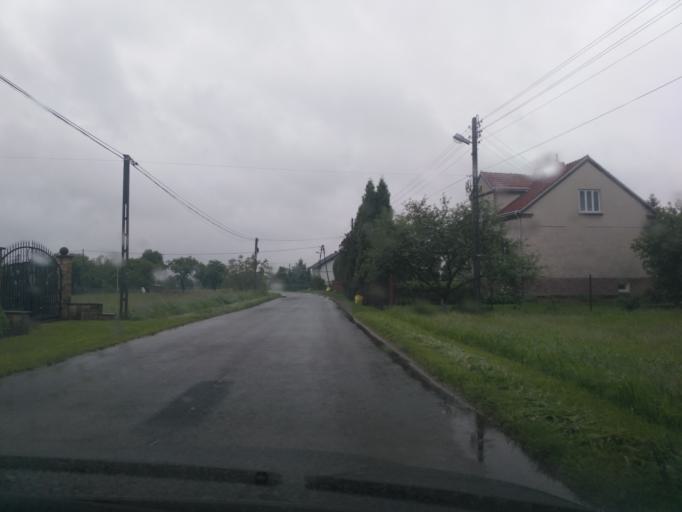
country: PL
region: Subcarpathian Voivodeship
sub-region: Powiat jasielski
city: Jaslo
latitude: 49.7440
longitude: 21.5109
